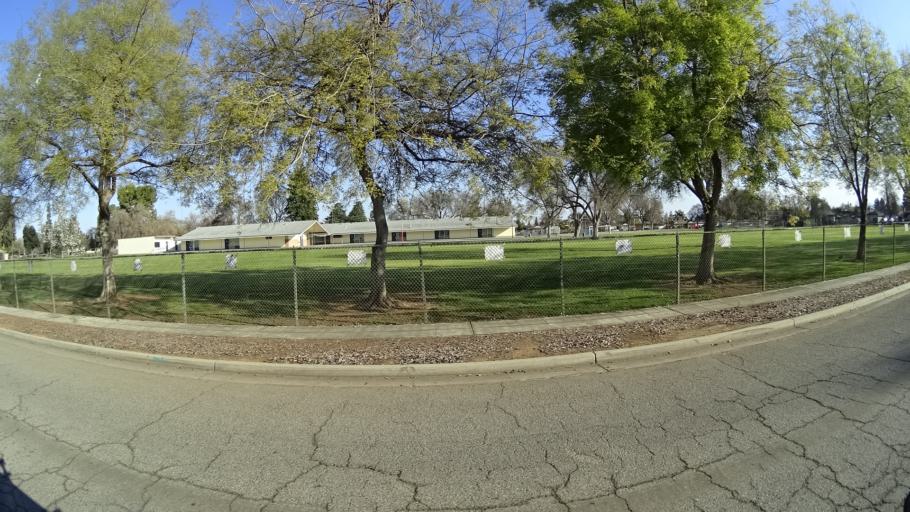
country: US
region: California
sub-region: Fresno County
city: Fresno
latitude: 36.8175
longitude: -119.7782
